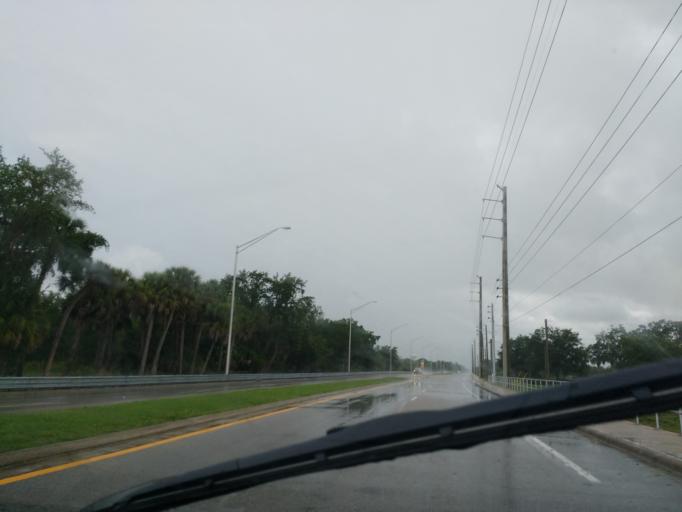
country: US
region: Florida
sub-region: Charlotte County
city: Charlotte Park
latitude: 26.8633
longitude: -82.0240
